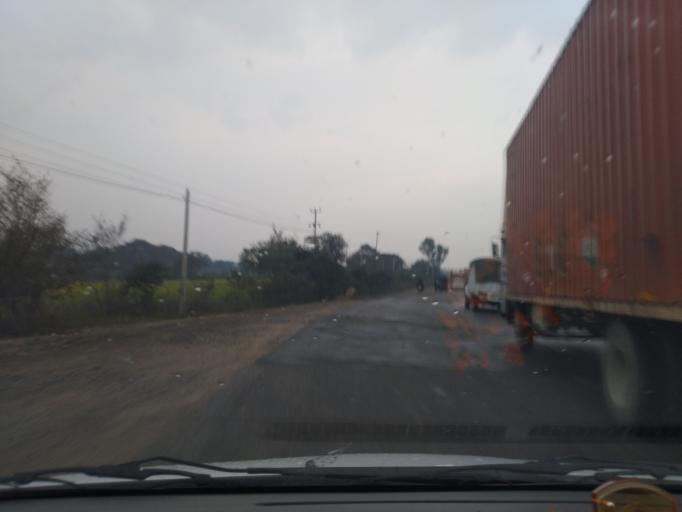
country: IN
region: Bihar
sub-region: Kaimur District
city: Bhabua
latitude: 25.1065
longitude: 83.7036
